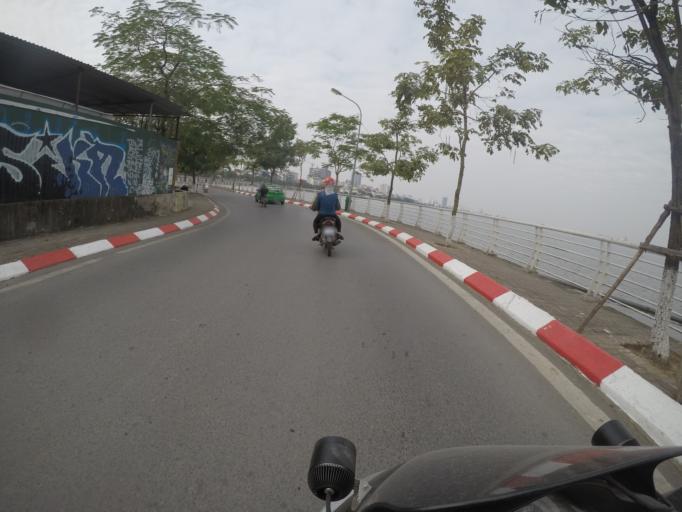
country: VN
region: Ha Noi
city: Tay Ho
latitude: 21.0562
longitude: 105.8103
